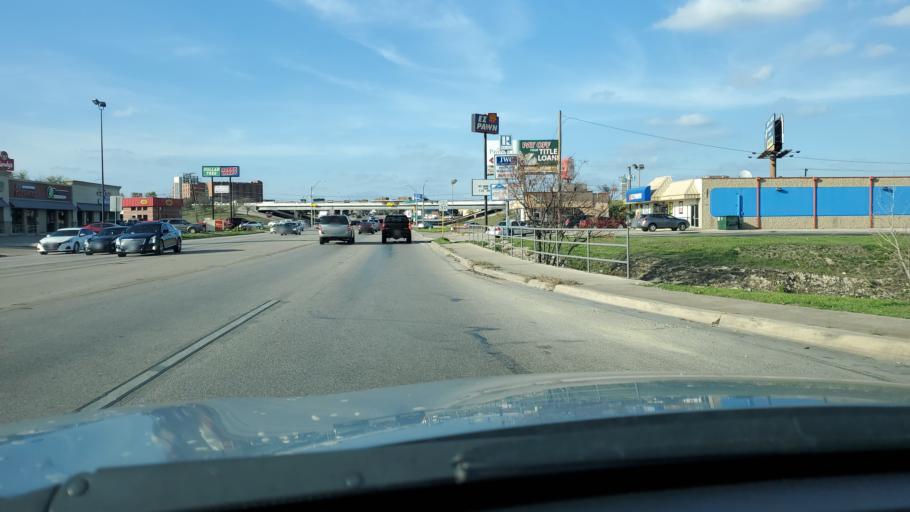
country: US
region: Texas
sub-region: Bell County
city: Killeen
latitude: 31.0888
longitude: -97.7202
